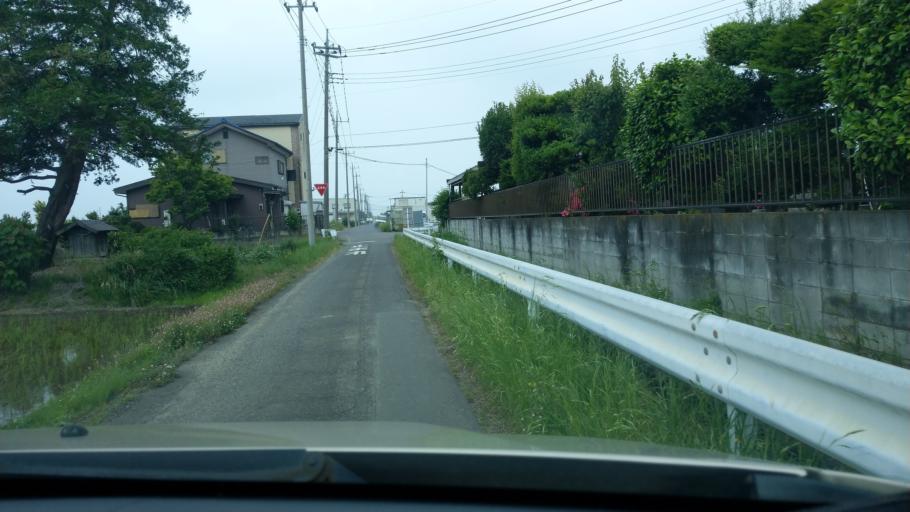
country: JP
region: Saitama
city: Yono
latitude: 35.8826
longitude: 139.5962
